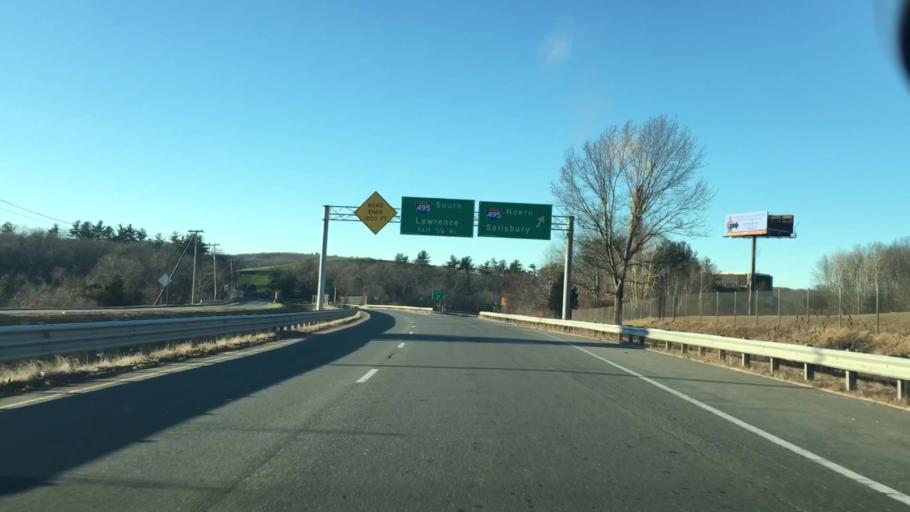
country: US
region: Massachusetts
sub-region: Essex County
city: Haverhill
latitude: 42.7607
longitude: -71.1192
